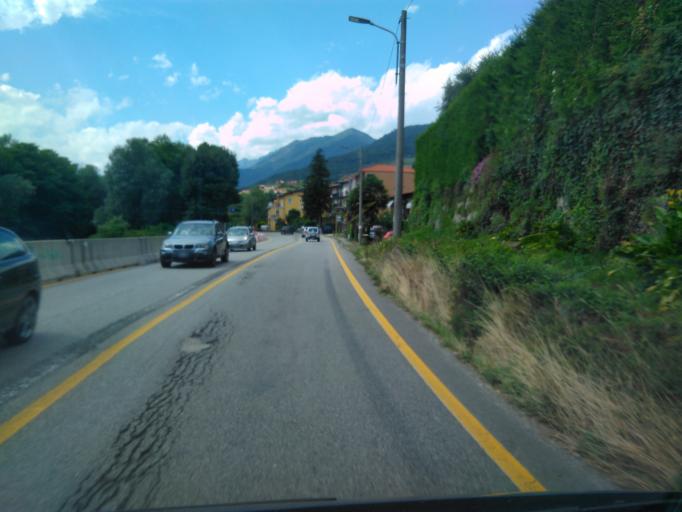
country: IT
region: Piedmont
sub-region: Provincia Verbano-Cusio-Ossola
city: Santino
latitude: 45.9417
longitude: 8.5031
